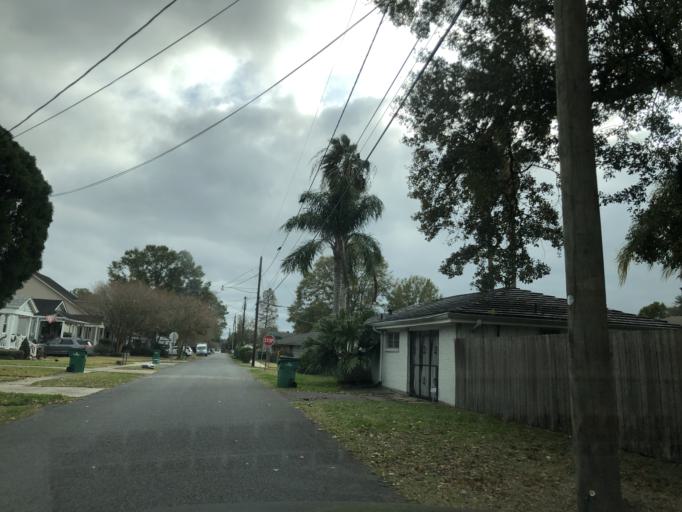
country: US
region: Louisiana
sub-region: Jefferson Parish
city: Metairie
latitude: 29.9867
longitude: -90.1589
